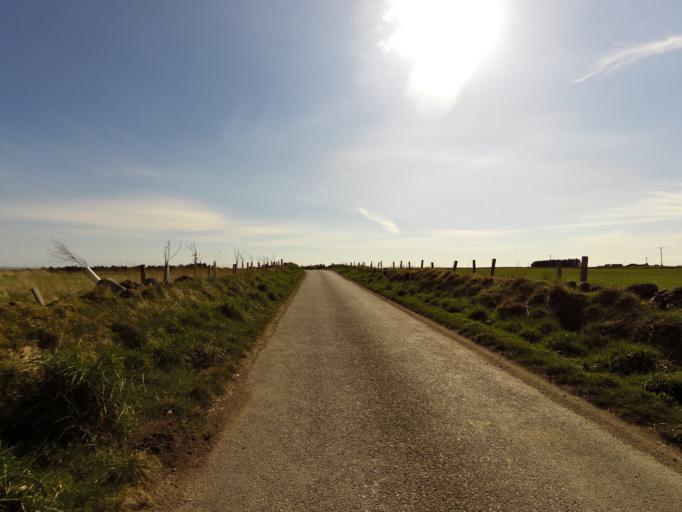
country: GB
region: Scotland
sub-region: Aberdeenshire
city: Portlethen
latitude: 57.0758
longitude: -2.1028
